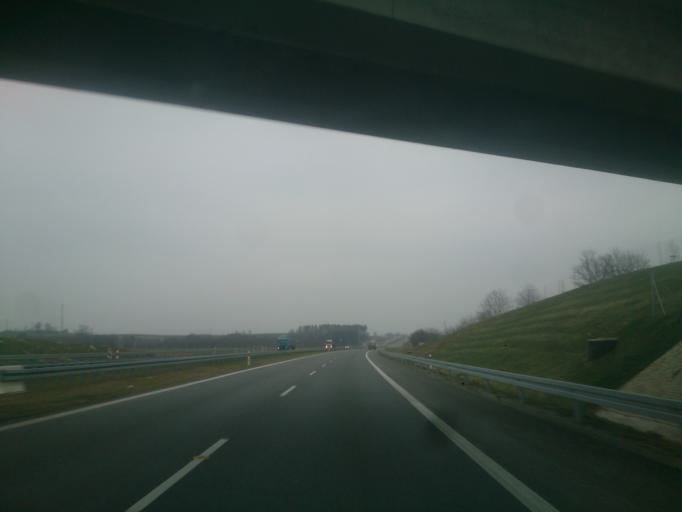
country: PL
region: Warmian-Masurian Voivodeship
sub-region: Powiat elblaski
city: Paslek
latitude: 54.0178
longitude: 19.6760
